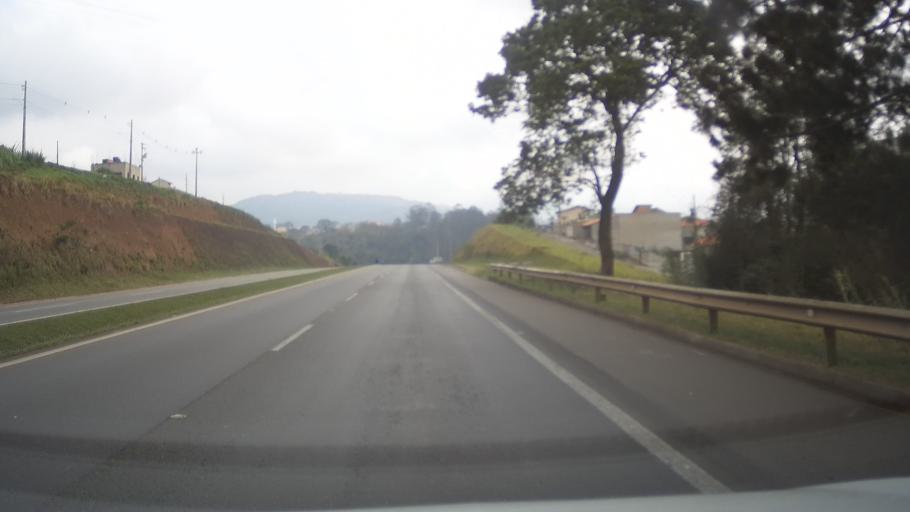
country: BR
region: Minas Gerais
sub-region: Extrema
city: Extrema
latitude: -22.8547
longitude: -46.3371
